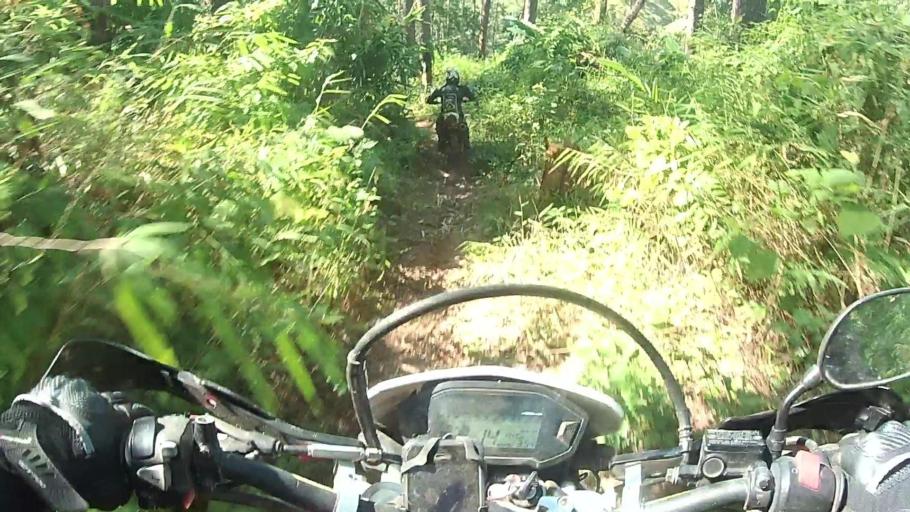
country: TH
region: Chiang Mai
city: Phrao
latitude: 19.3732
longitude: 99.3184
